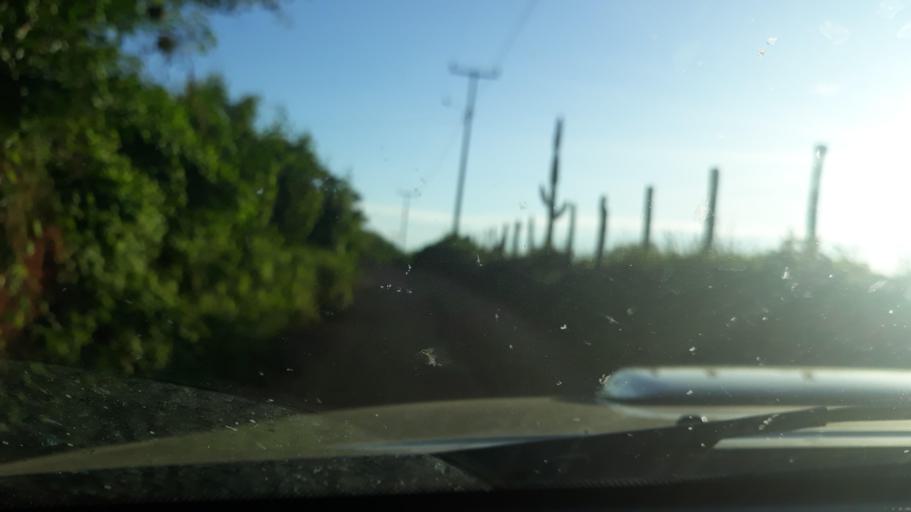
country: BR
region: Bahia
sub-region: Riacho De Santana
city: Riacho de Santana
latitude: -13.8417
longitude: -42.7375
